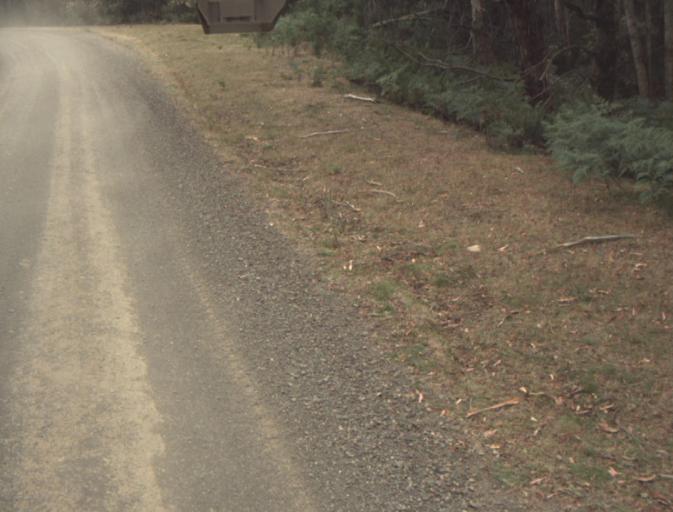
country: AU
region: Tasmania
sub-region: Dorset
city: Scottsdale
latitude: -41.4485
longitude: 147.5228
